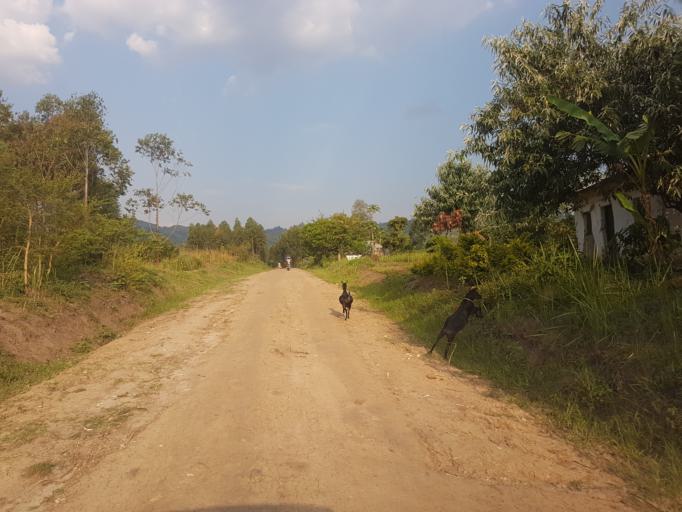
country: UG
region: Western Region
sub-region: Rukungiri District
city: Rukungiri
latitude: -0.6728
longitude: 29.8887
